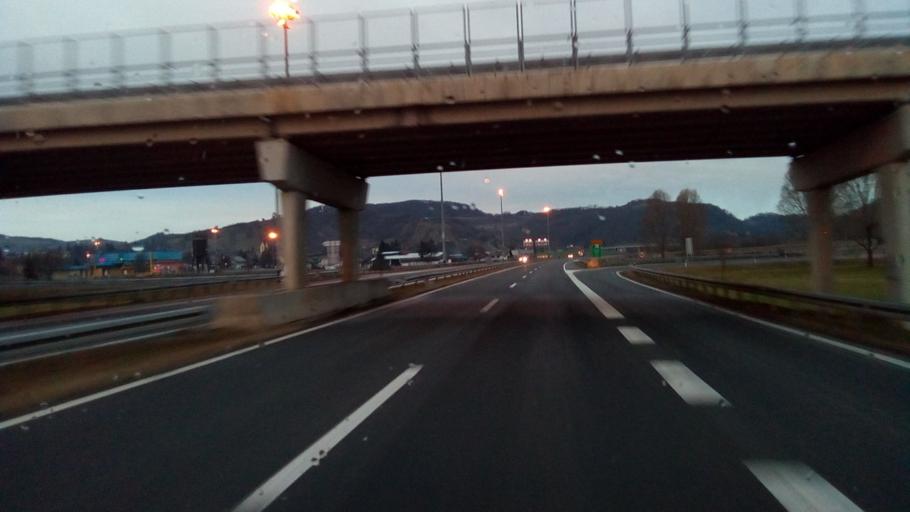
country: HR
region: Varazdinska
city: Remetinec
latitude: 46.0983
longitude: 16.2839
